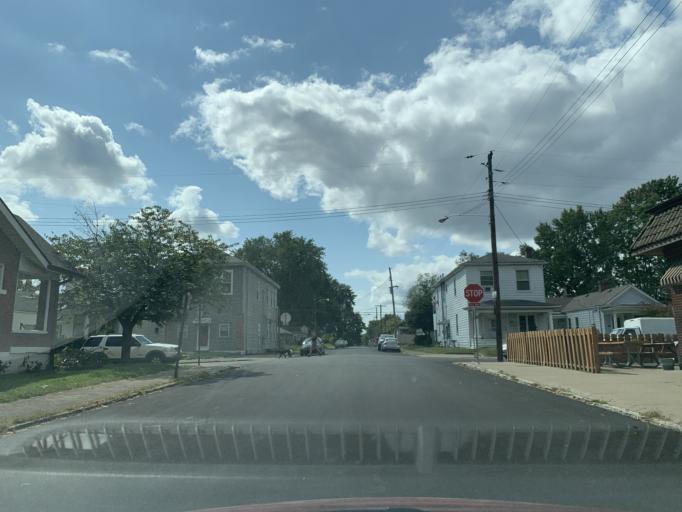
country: US
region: Kentucky
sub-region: Jefferson County
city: Audubon Park
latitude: 38.2303
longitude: -85.7353
